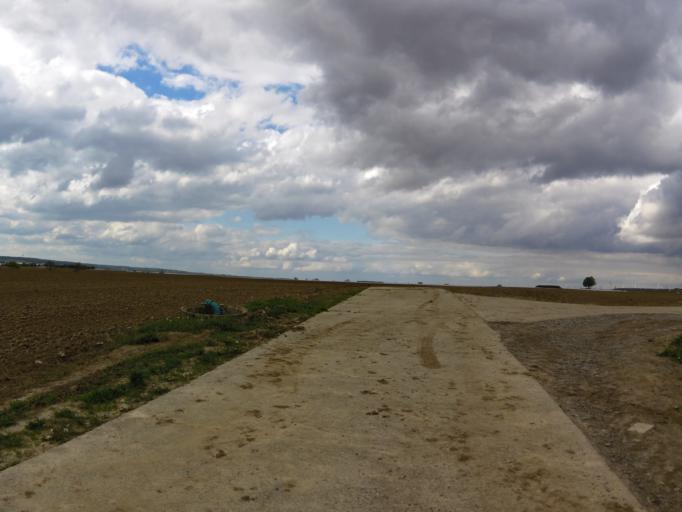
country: DE
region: Bavaria
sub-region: Regierungsbezirk Unterfranken
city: Oberpleichfeld
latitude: 49.8626
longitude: 10.0784
